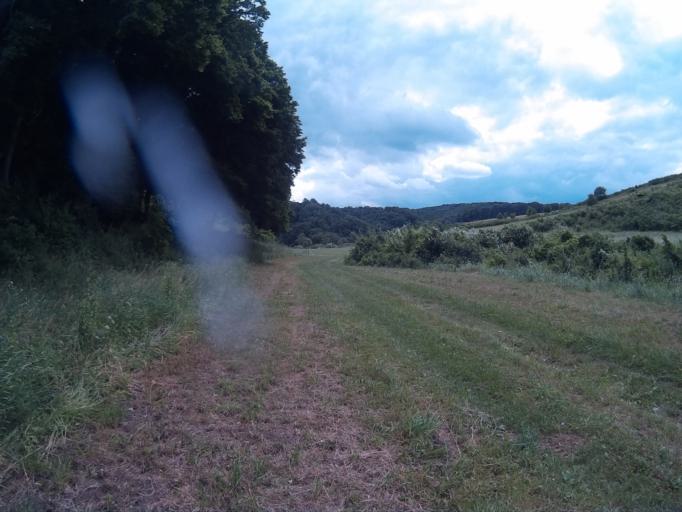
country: HU
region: Veszprem
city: Herend
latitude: 47.1054
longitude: 17.7463
